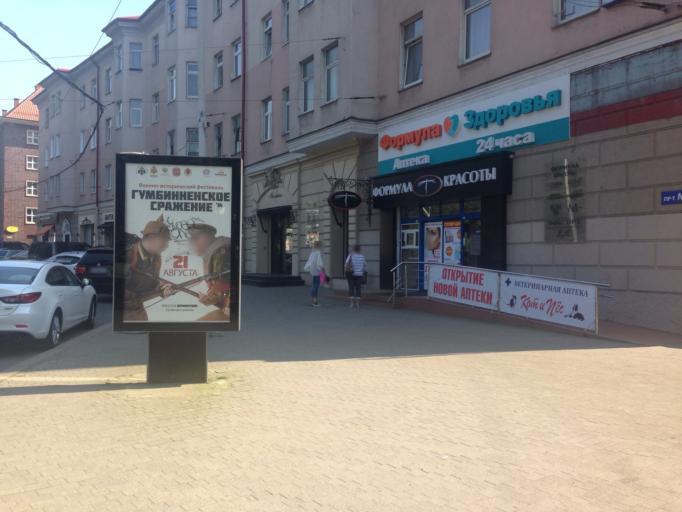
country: RU
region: Kaliningrad
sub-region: Gorod Kaliningrad
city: Kaliningrad
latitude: 54.7199
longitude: 20.4854
